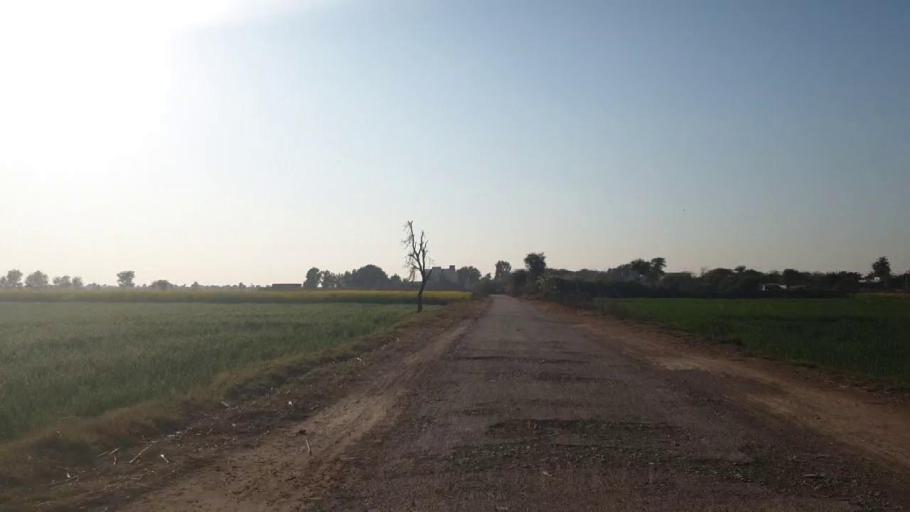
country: PK
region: Sindh
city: Shahpur Chakar
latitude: 26.0613
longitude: 68.6719
